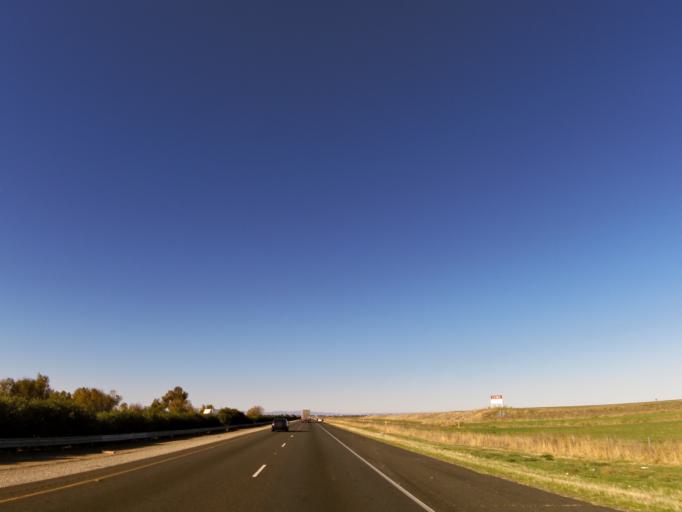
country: US
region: California
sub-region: Yolo County
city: West Sacramento
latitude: 38.6714
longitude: -121.5587
